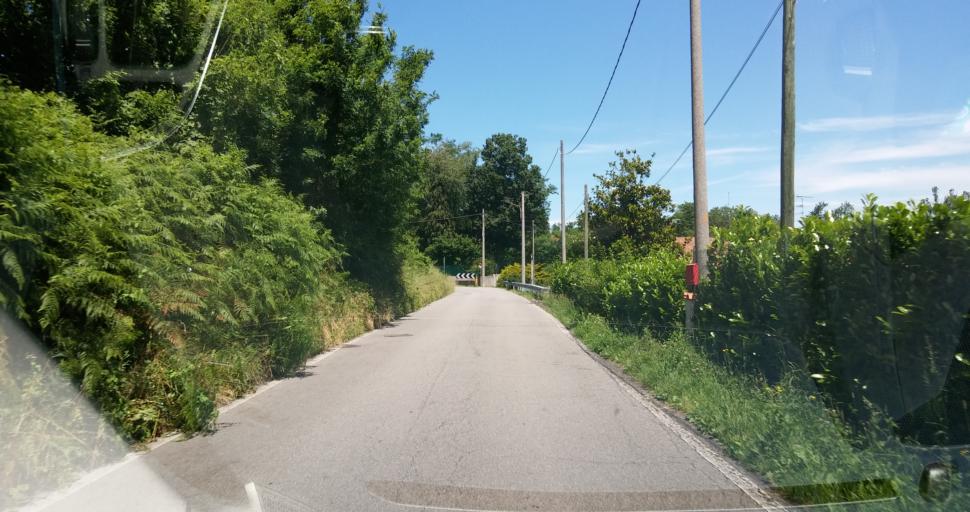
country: IT
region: Lombardy
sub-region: Provincia di Varese
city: Cimbro
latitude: 45.7311
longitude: 8.7265
